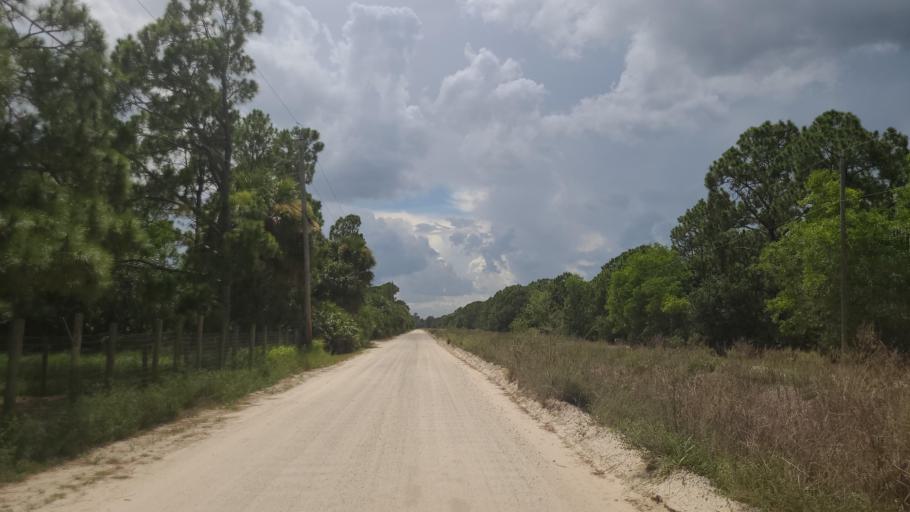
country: US
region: Florida
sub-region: Indian River County
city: Fellsmere
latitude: 27.7393
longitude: -80.6037
